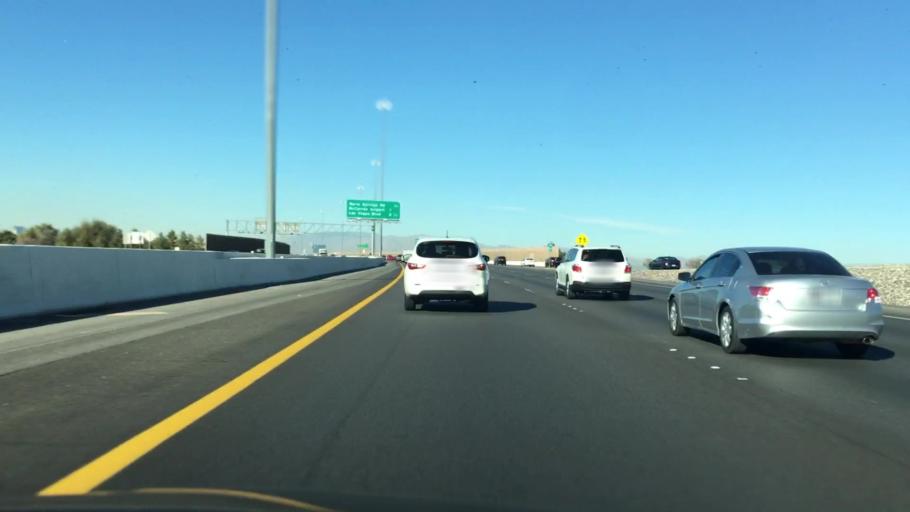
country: US
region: Nevada
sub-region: Clark County
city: Paradise
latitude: 36.0441
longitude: -115.1340
